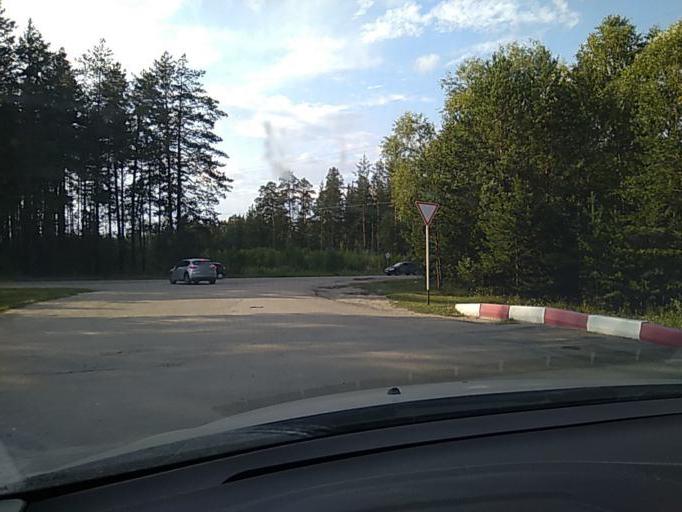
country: RU
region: Chelyabinsk
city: Kyshtym
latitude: 55.6795
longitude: 60.5629
